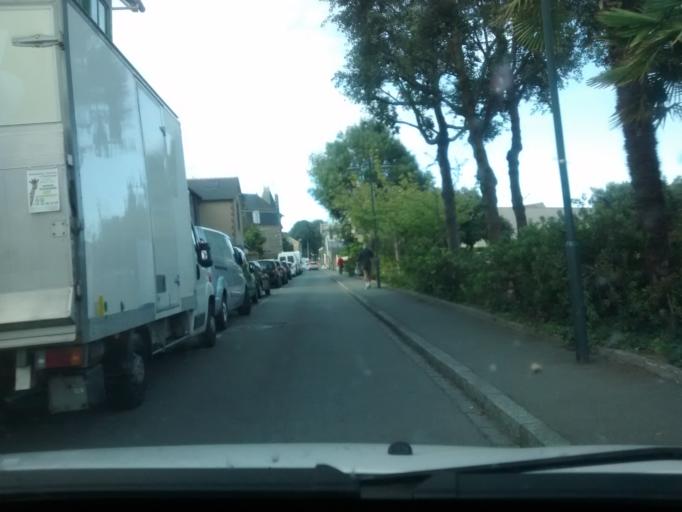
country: FR
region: Brittany
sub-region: Departement d'Ille-et-Vilaine
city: Dinard
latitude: 48.6315
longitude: -2.0597
